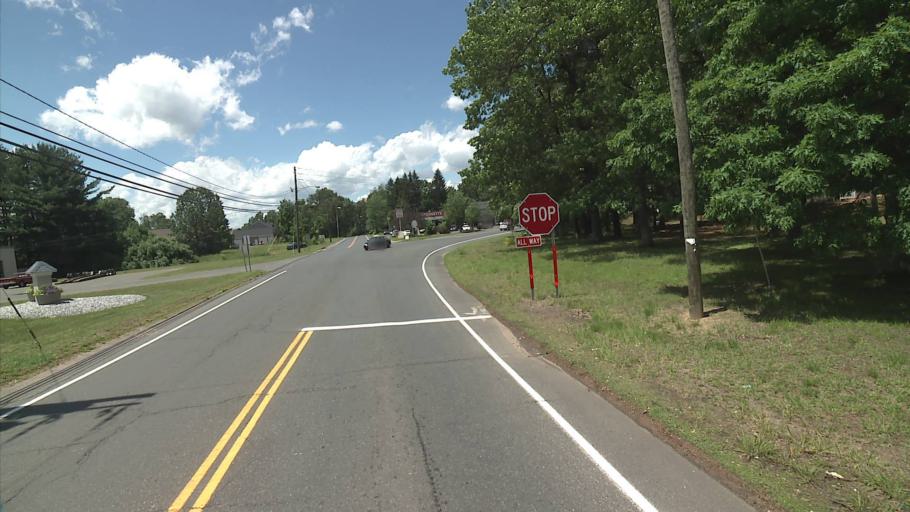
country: US
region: Connecticut
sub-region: Hartford County
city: Sherwood Manor
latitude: 42.0221
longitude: -72.5423
